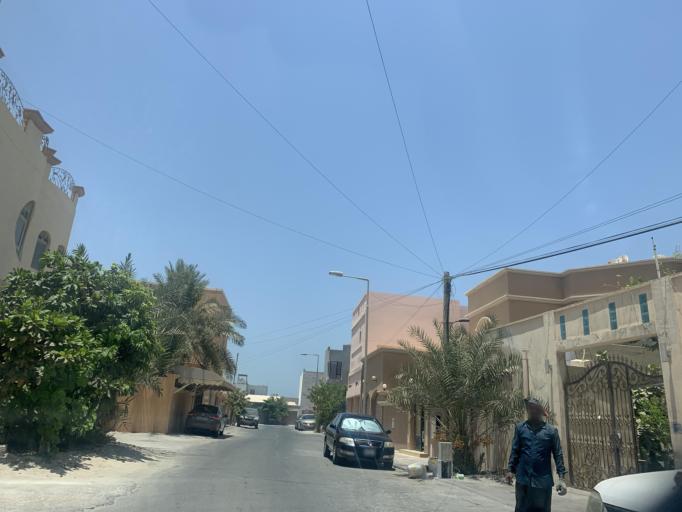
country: BH
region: Muharraq
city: Al Muharraq
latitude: 26.2864
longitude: 50.6210
